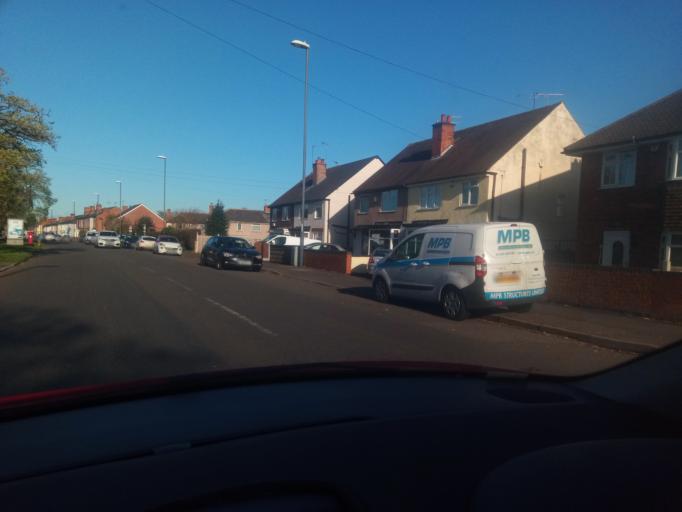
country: GB
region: England
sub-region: Derby
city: Derby
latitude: 52.8868
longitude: -1.4501
